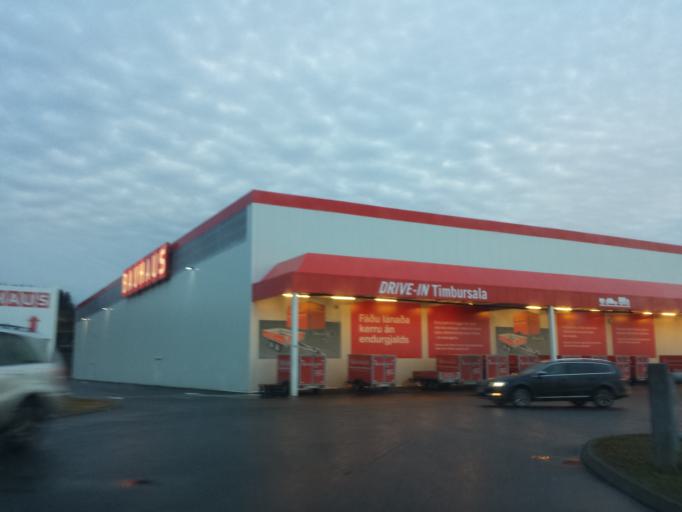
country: IS
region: Capital Region
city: Mosfellsbaer
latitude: 64.1419
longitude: -21.7521
